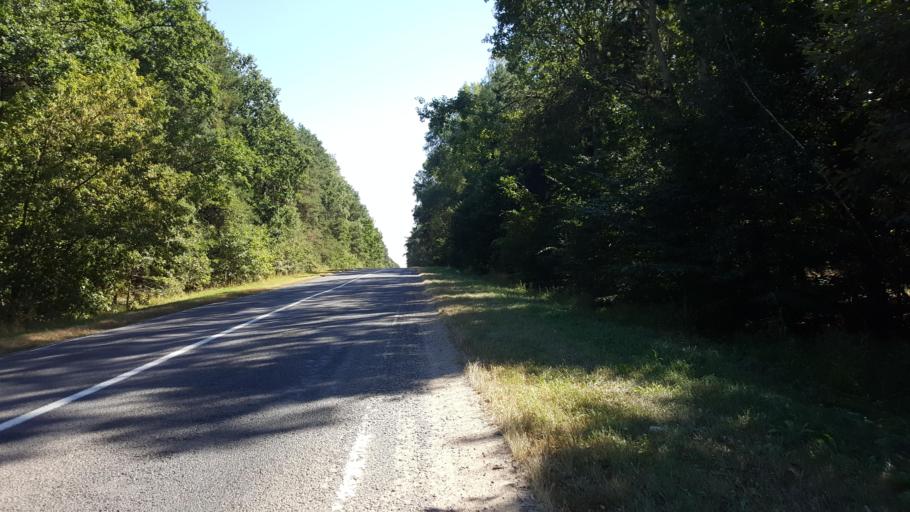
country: PL
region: Lublin Voivodeship
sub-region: Powiat bialski
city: Terespol
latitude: 52.2291
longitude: 23.5147
